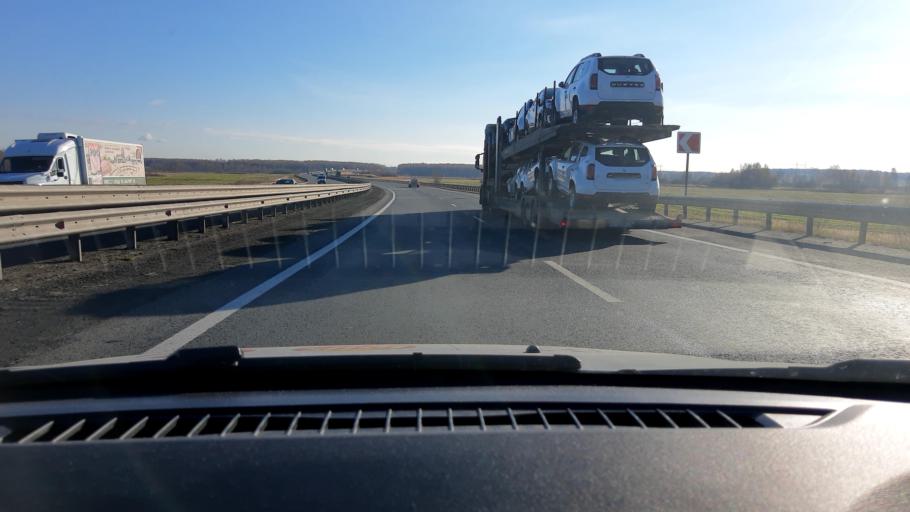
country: RU
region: Nizjnij Novgorod
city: Burevestnik
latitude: 56.1258
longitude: 43.7893
